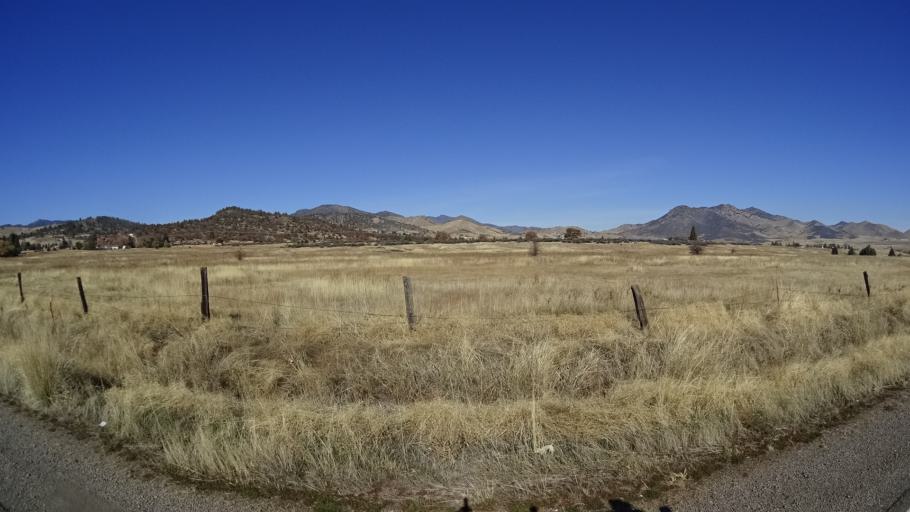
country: US
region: California
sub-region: Siskiyou County
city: Yreka
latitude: 41.7420
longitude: -122.5954
